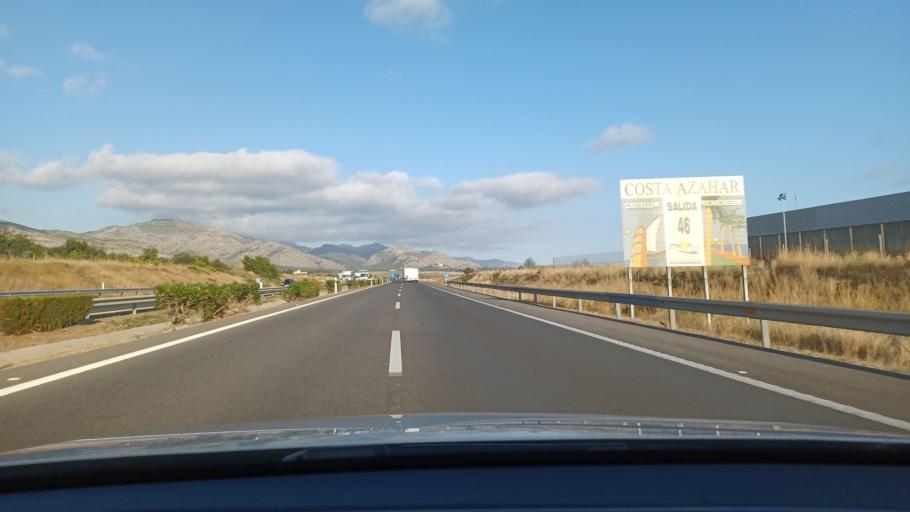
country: ES
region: Valencia
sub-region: Provincia de Castello
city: Castello de la Plana
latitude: 40.0131
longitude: -0.0472
